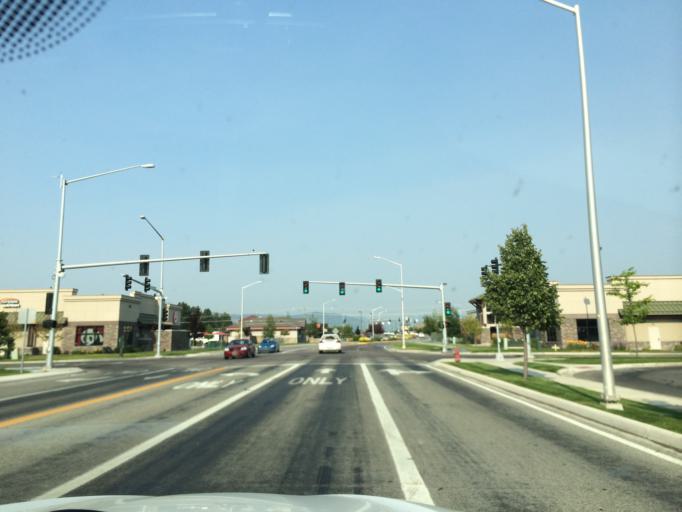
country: US
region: Montana
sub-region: Flathead County
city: Kalispell
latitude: 48.2330
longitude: -114.3271
